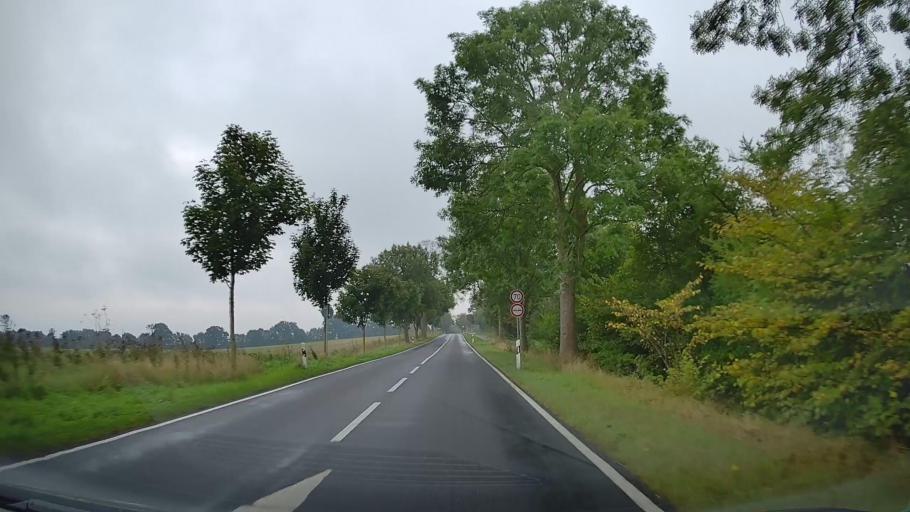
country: DE
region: Mecklenburg-Vorpommern
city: Ostseebad Boltenhagen
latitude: 53.9447
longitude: 11.2367
